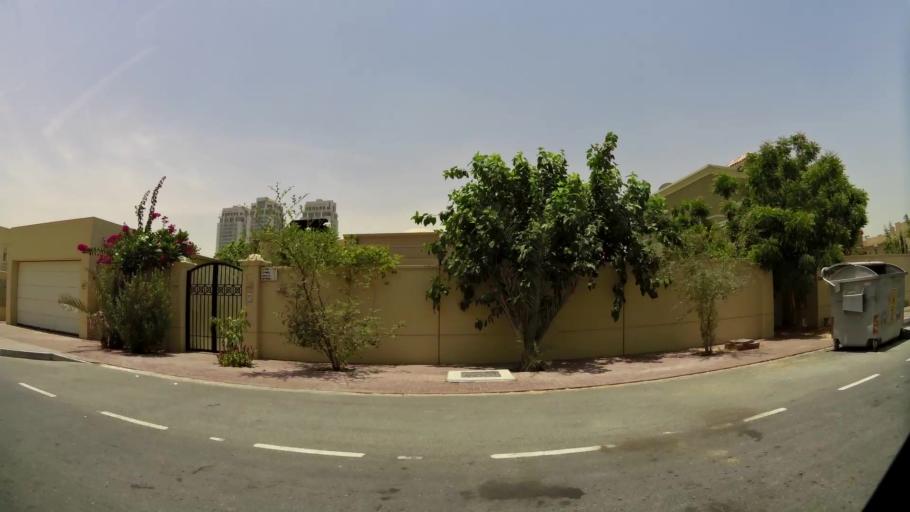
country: AE
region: Dubai
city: Dubai
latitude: 25.0833
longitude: 55.2437
